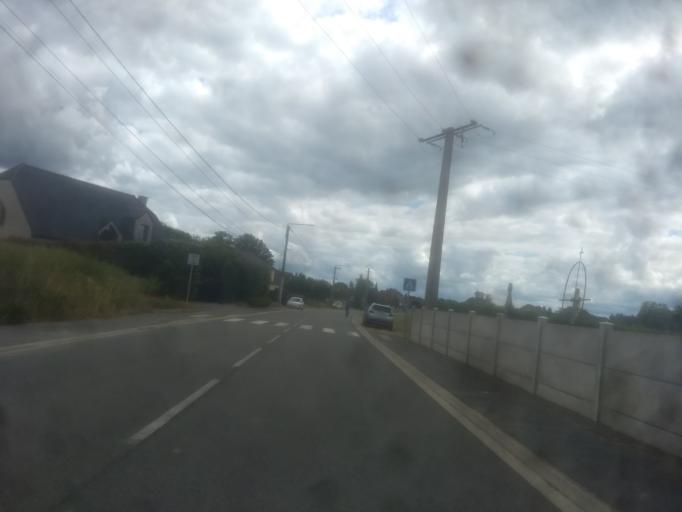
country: FR
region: Nord-Pas-de-Calais
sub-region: Departement du Pas-de-Calais
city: Agny
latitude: 50.2139
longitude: 2.7749
